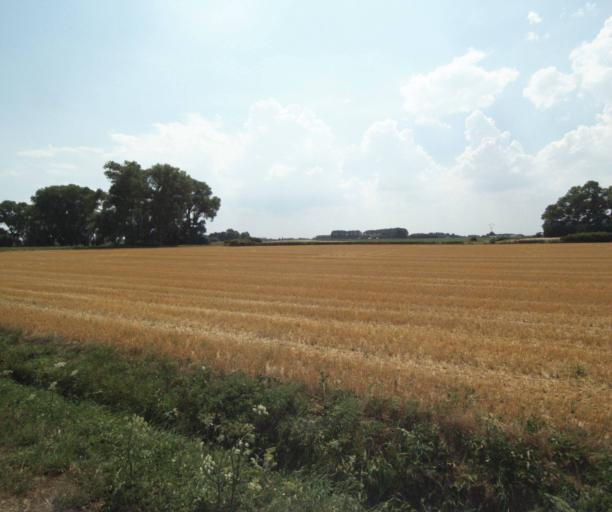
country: FR
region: Nord-Pas-de-Calais
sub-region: Departement du Nord
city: Quesnoy-sur-Deule
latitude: 50.7323
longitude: 2.9904
